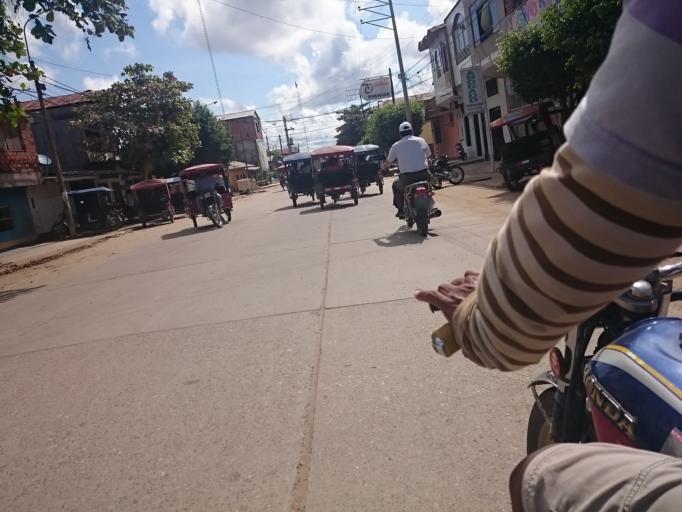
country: PE
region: Ucayali
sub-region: Provincia de Coronel Portillo
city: Pucallpa
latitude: -8.3762
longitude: -74.5358
